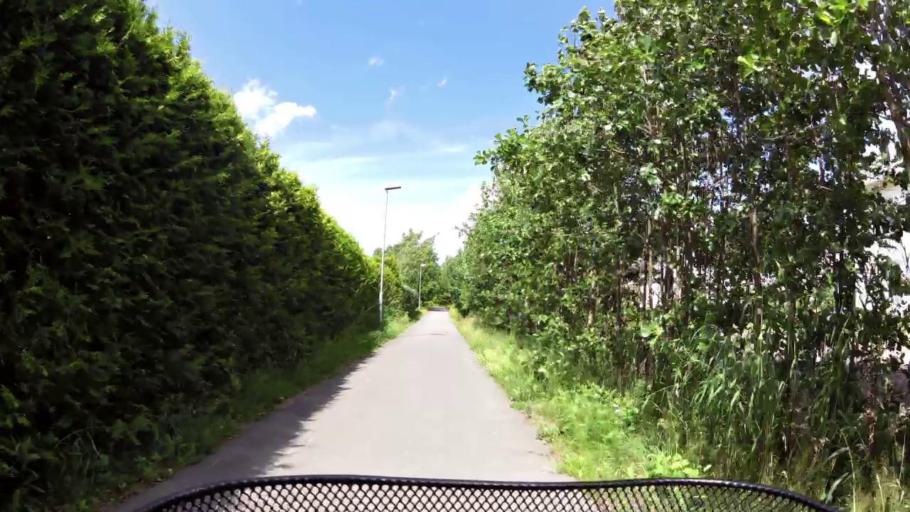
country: SE
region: OEstergoetland
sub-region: Linkopings Kommun
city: Ekangen
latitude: 58.4741
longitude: 15.6403
